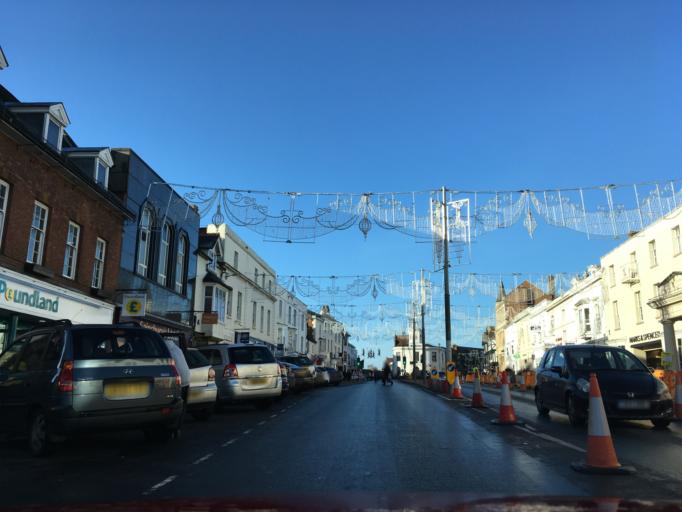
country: GB
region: England
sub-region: Warwickshire
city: Stratford-upon-Avon
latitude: 52.1927
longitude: -1.7047
